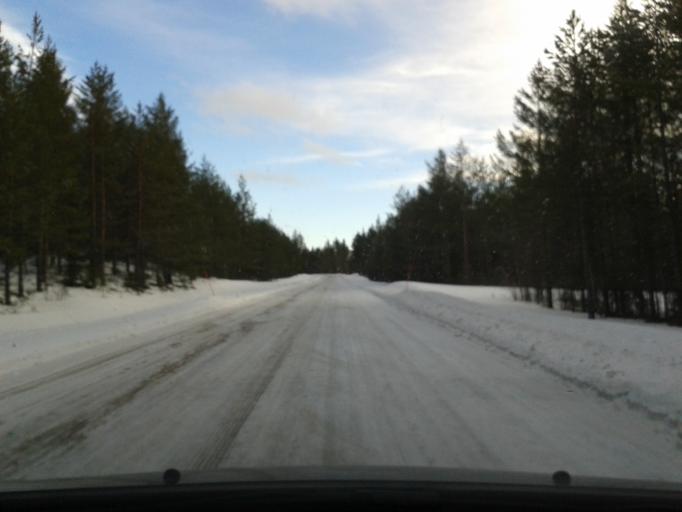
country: SE
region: Vaesterbotten
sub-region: Asele Kommun
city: Asele
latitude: 64.2514
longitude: 17.2744
